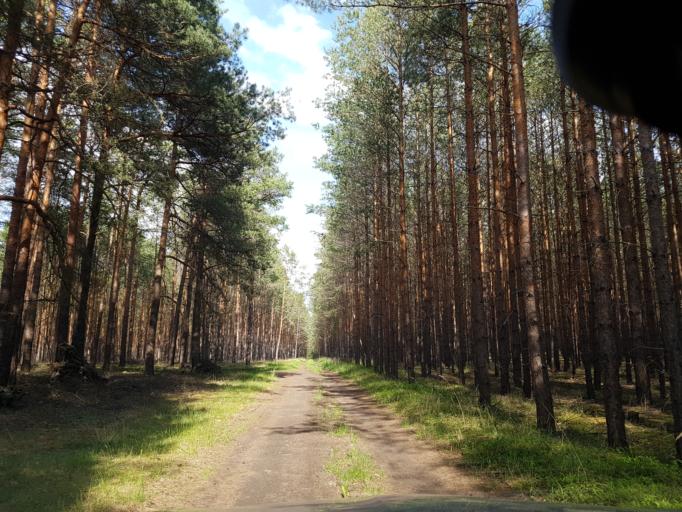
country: DE
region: Brandenburg
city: Schonewalde
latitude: 51.6364
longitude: 13.6360
